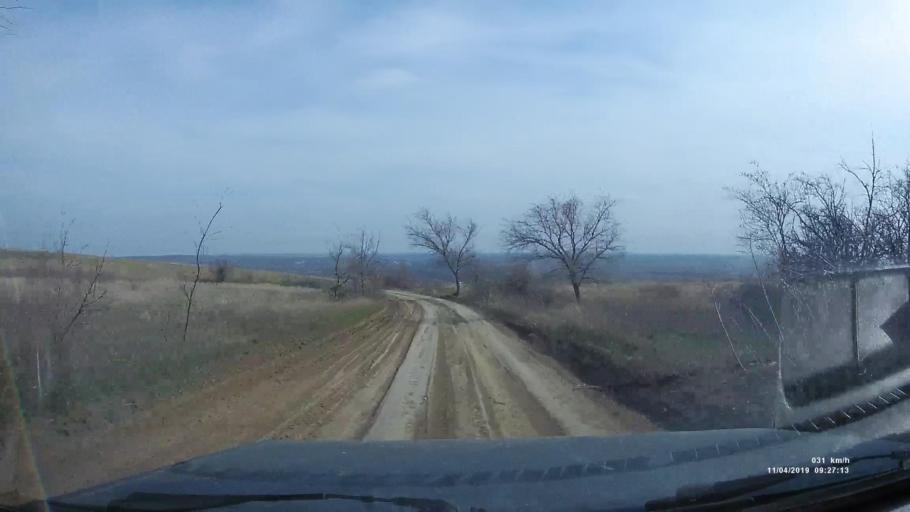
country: RU
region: Rostov
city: Staraya Stanitsa
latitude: 48.2655
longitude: 40.3662
